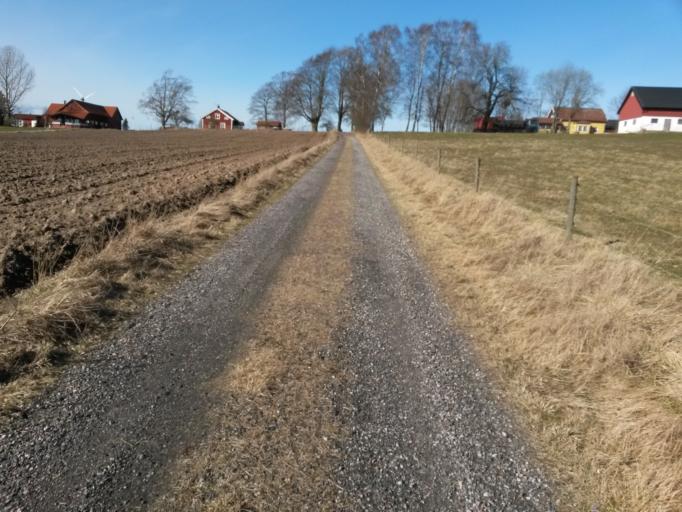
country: SE
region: Vaestra Goetaland
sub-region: Vargarda Kommun
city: Jonstorp
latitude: 57.9781
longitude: 12.6530
